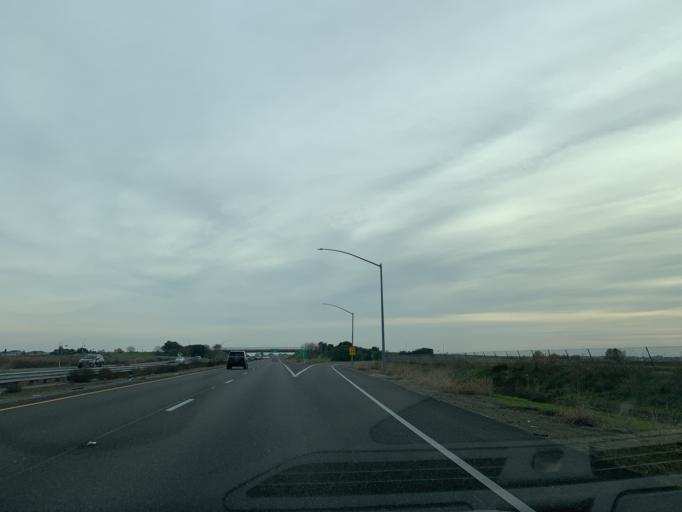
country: US
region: California
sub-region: Sacramento County
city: Elverta
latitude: 38.6899
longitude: -121.5403
